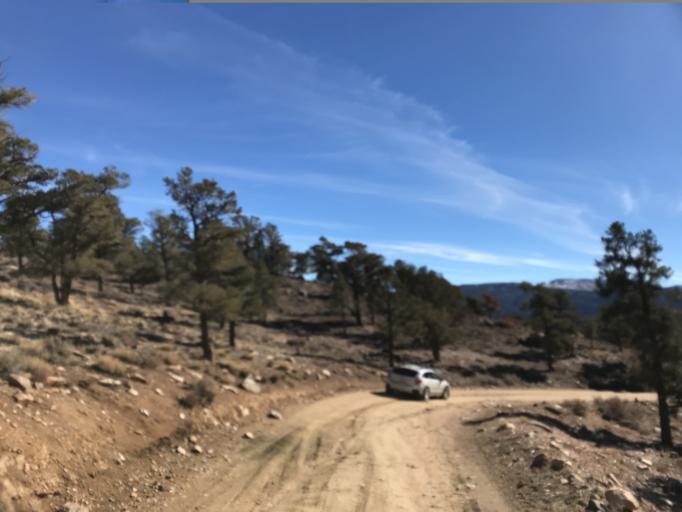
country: US
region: California
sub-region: San Bernardino County
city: Big Bear City
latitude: 34.2726
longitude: -116.7702
